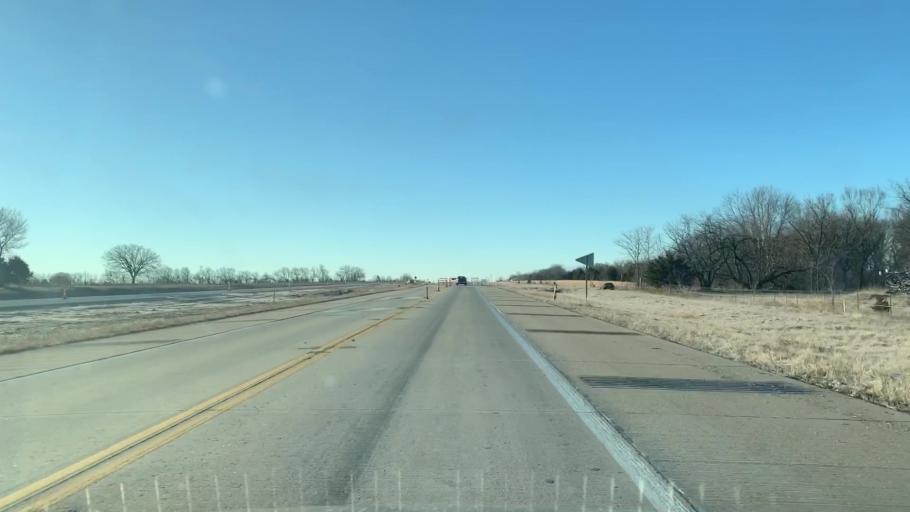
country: US
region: Kansas
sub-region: Bourbon County
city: Fort Scott
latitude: 37.7550
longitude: -94.7051
